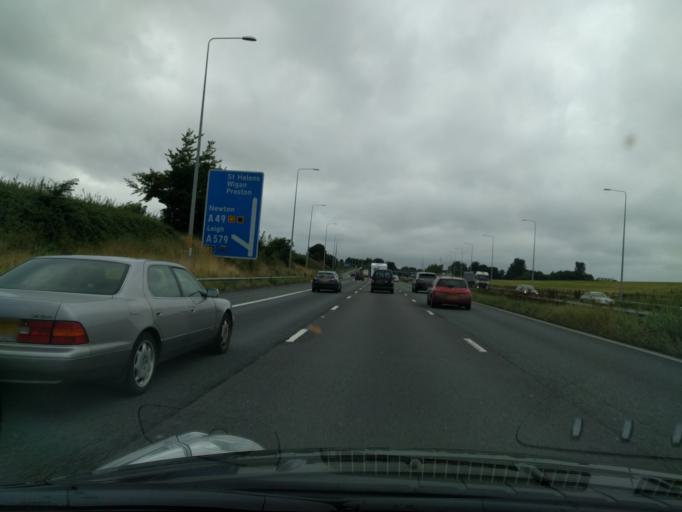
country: GB
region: England
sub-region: Warrington
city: Winwick
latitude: 53.4366
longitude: -2.5770
